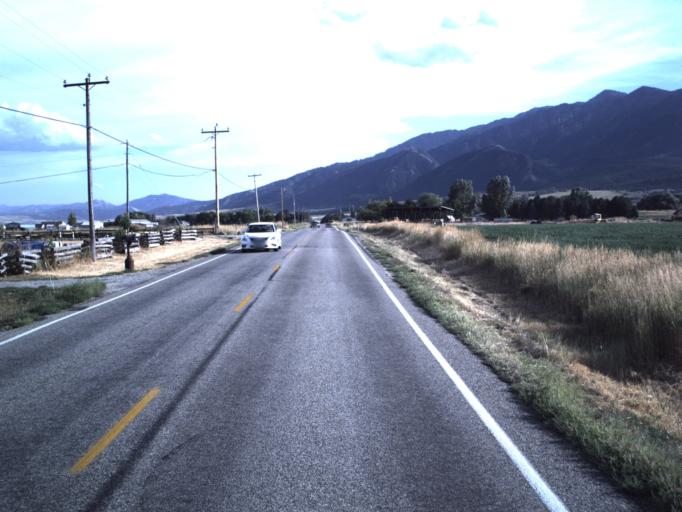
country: US
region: Utah
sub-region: Cache County
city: Mendon
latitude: 41.7292
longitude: -111.9792
